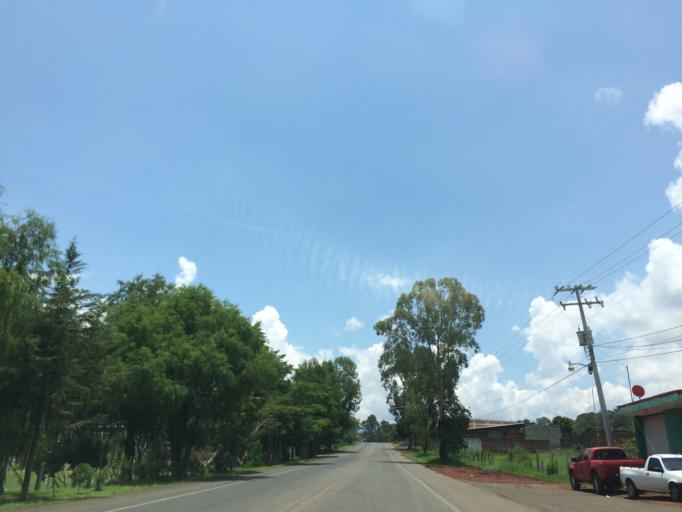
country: MX
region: Michoacan
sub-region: Periban
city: San Francisco Periban
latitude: 19.5493
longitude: -102.4053
